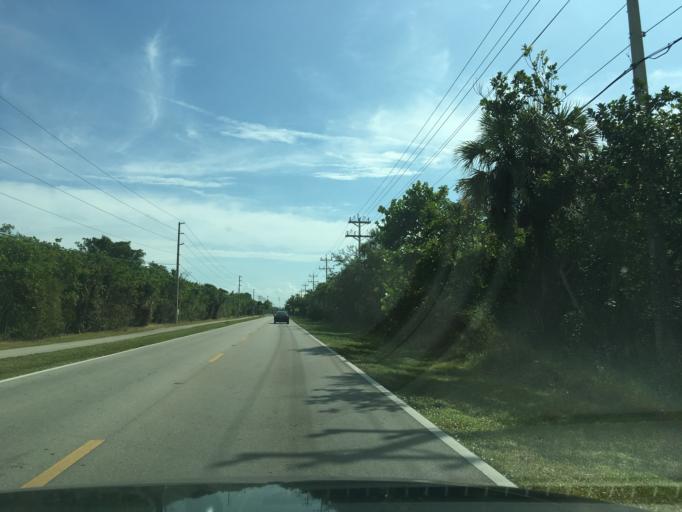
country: US
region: Florida
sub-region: Lee County
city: Saint James City
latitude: 26.4484
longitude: -82.1209
